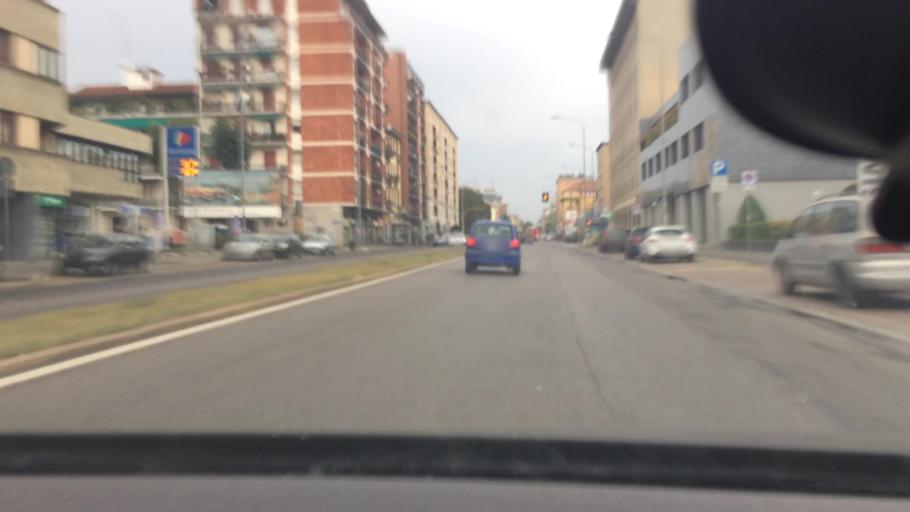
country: IT
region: Lombardy
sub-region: Citta metropolitana di Milano
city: Sesto San Giovanni
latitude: 45.5160
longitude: 9.2259
